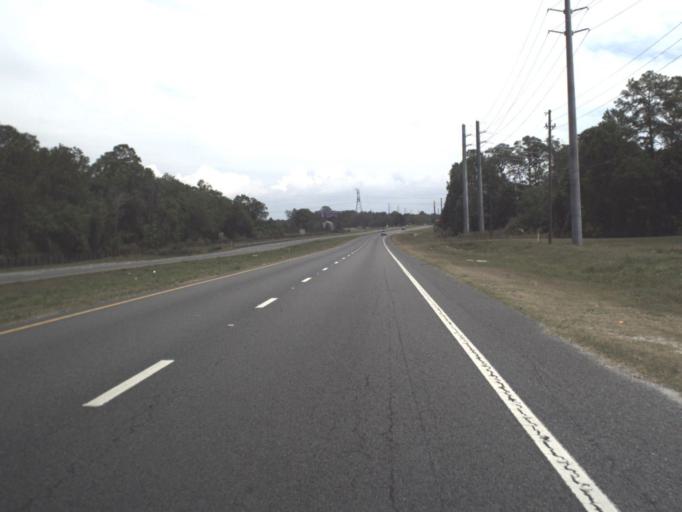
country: US
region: Florida
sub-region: Lake County
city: Fruitland Park
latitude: 28.8227
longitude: -81.9649
